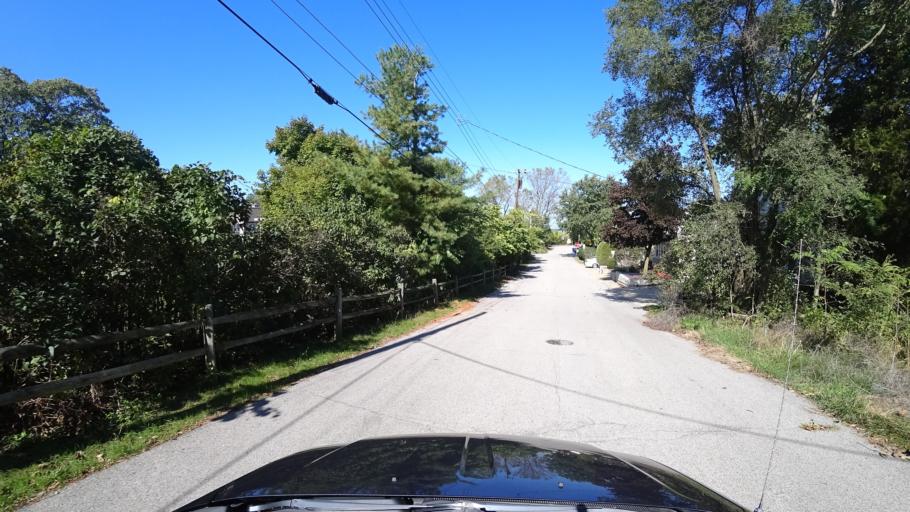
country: US
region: Indiana
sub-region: LaPorte County
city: Michigan City
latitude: 41.7304
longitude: -86.8889
